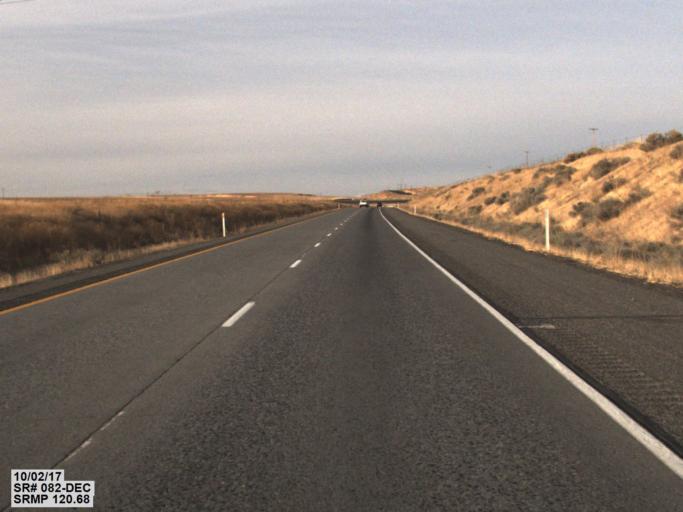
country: US
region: Washington
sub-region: Benton County
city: Highland
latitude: 46.0554
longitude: -119.2238
